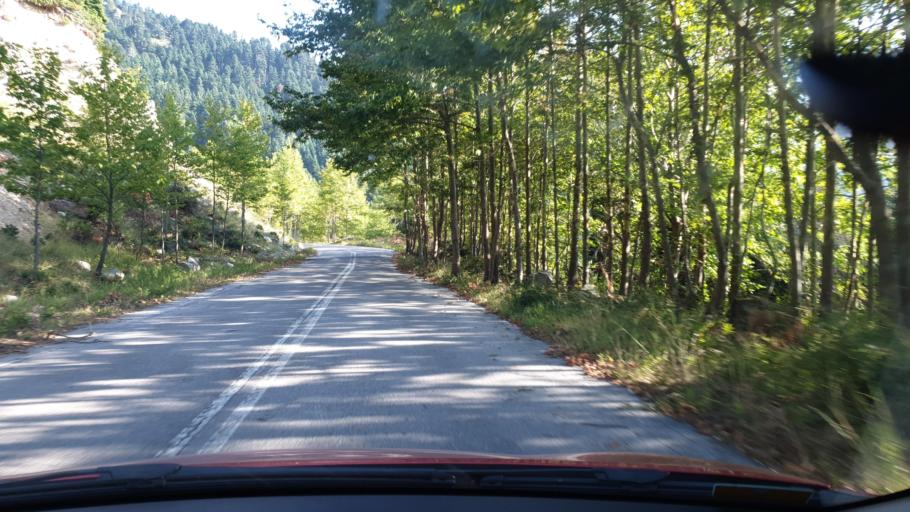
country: GR
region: Central Greece
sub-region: Nomos Evvoias
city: Yimnon
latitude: 38.6086
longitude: 23.9186
